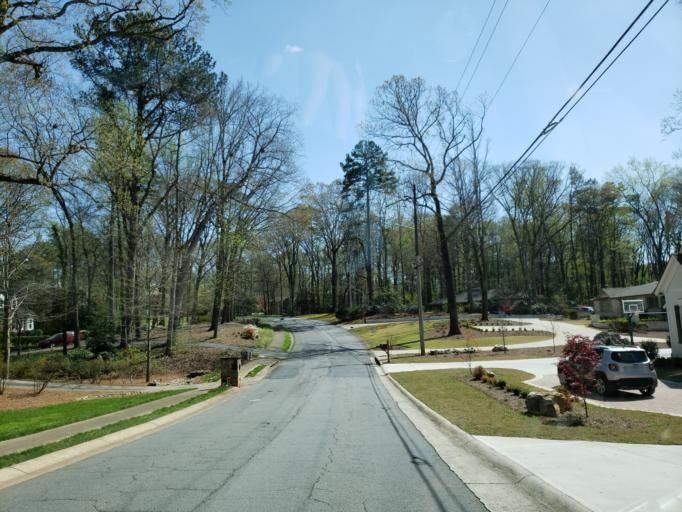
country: US
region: Georgia
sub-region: Cobb County
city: Marietta
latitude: 33.9650
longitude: -84.5649
